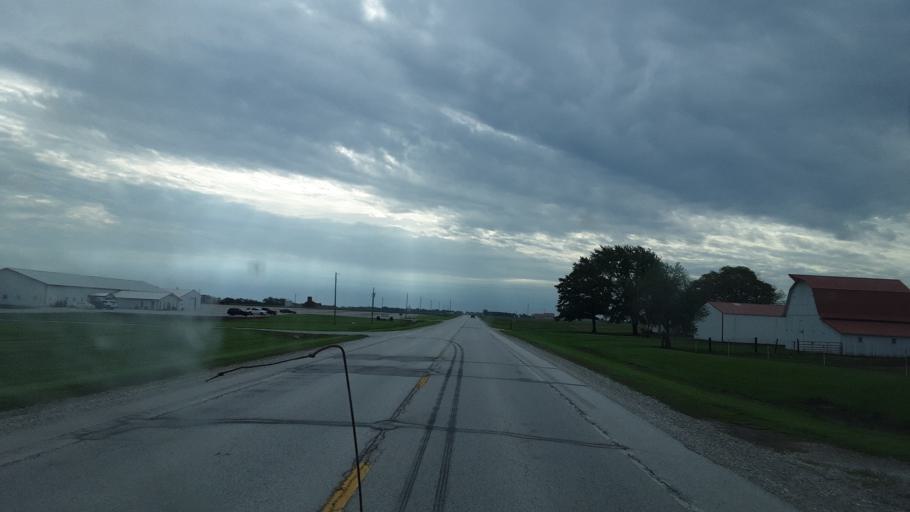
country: US
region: Illinois
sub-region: Hancock County
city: Hamilton
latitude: 40.3958
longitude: -91.3016
